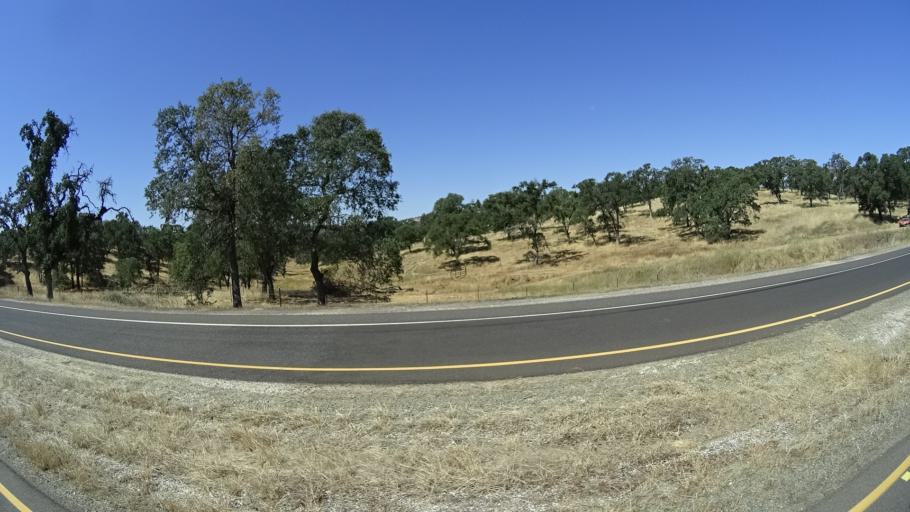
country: US
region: California
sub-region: Calaveras County
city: Copperopolis
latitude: 37.9633
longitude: -120.6543
